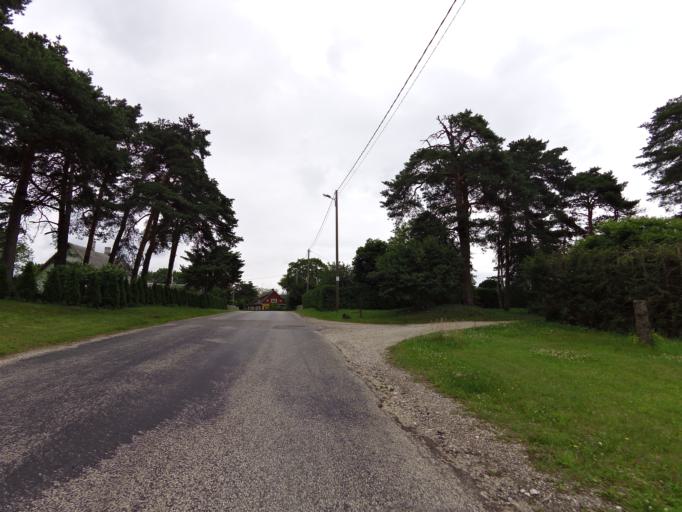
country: EE
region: Harju
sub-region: Nissi vald
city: Turba
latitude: 58.9961
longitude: 24.0576
